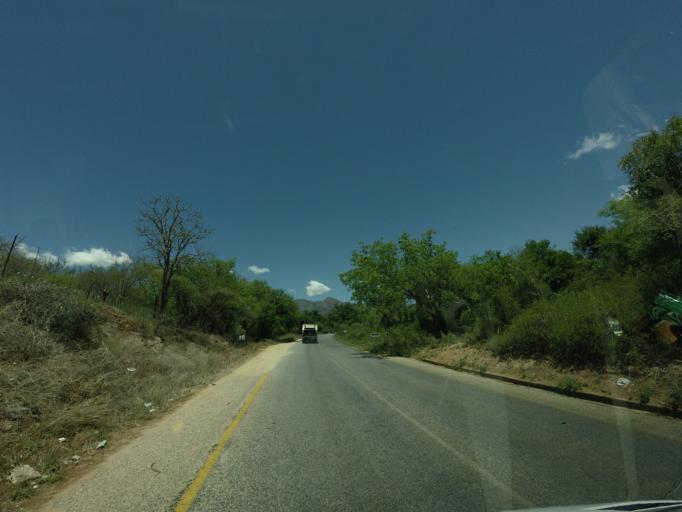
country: ZA
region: Limpopo
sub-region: Mopani District Municipality
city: Hoedspruit
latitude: -24.4064
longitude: 30.7966
